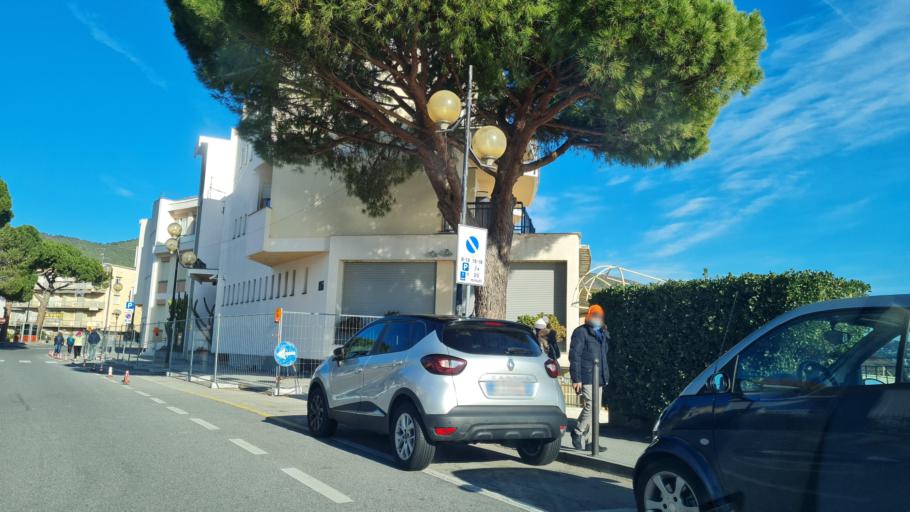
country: IT
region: Liguria
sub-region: Provincia di Savona
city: Spotorno
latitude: 44.2226
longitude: 8.4157
